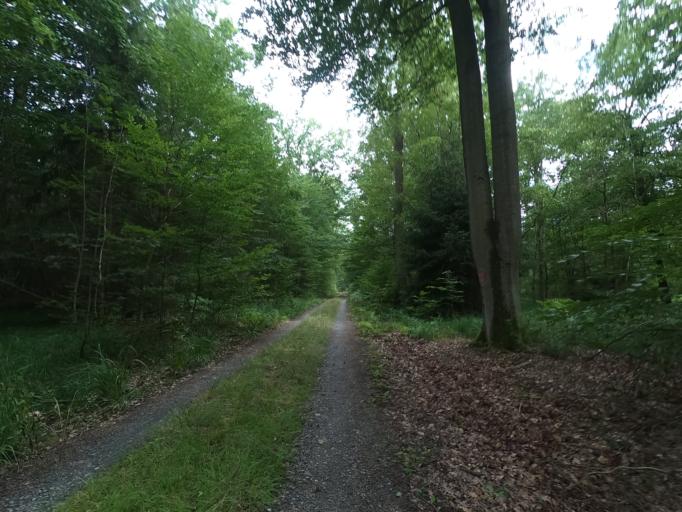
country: DE
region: Hesse
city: Langen
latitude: 50.0173
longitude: 8.6522
